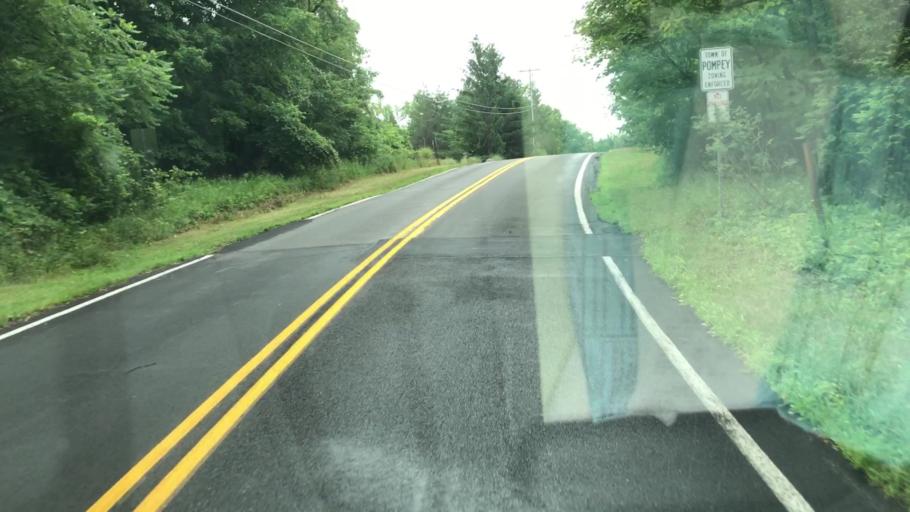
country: US
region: New York
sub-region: Onondaga County
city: Manlius
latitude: 42.9868
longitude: -75.9840
